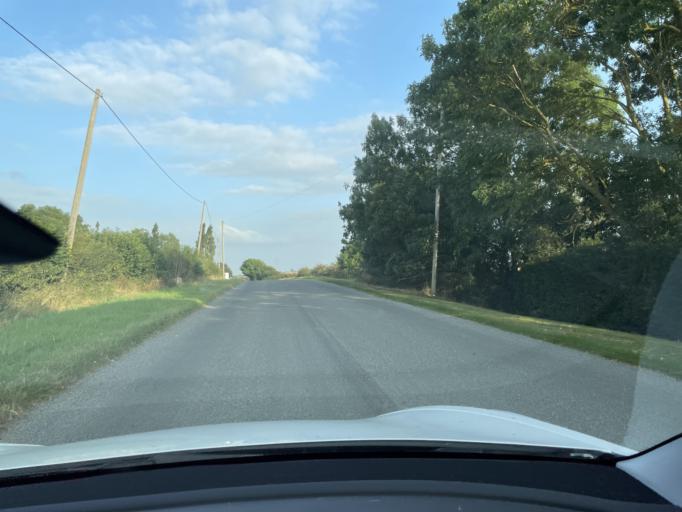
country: GB
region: England
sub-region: Bedford
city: Swineshead
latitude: 52.3670
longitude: -0.4419
